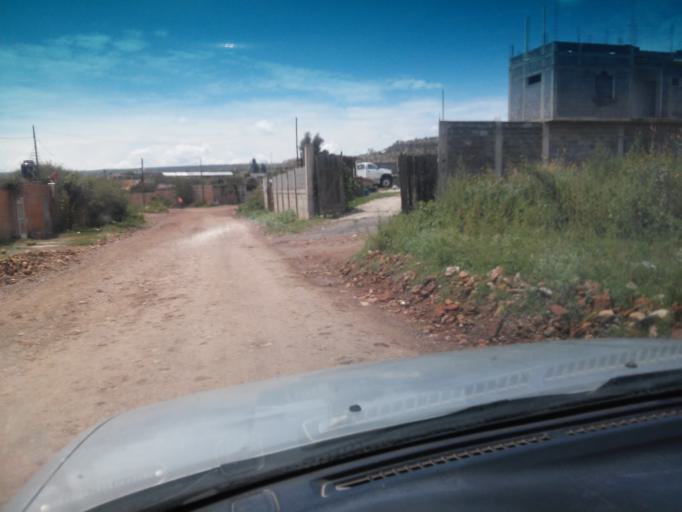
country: MX
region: Durango
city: Victoria de Durango
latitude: 23.9918
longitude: -104.7111
